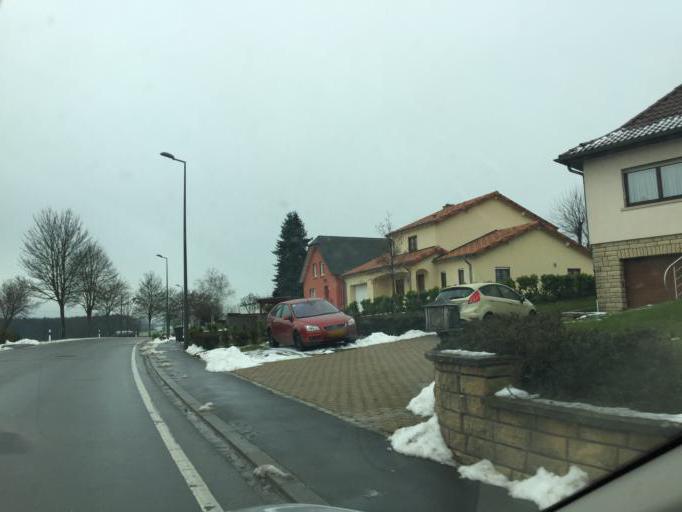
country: LU
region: Diekirch
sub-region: Canton de Diekirch
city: Mertzig
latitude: 49.8296
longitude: 5.9967
